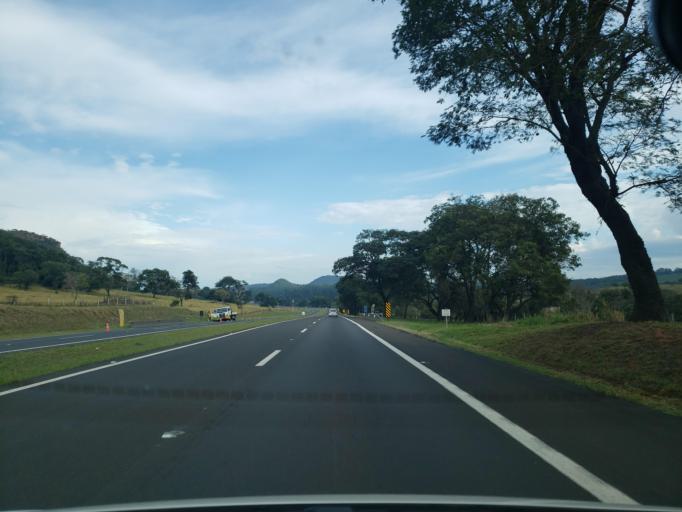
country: BR
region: Sao Paulo
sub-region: Itirapina
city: Itirapina
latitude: -22.2742
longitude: -47.9497
